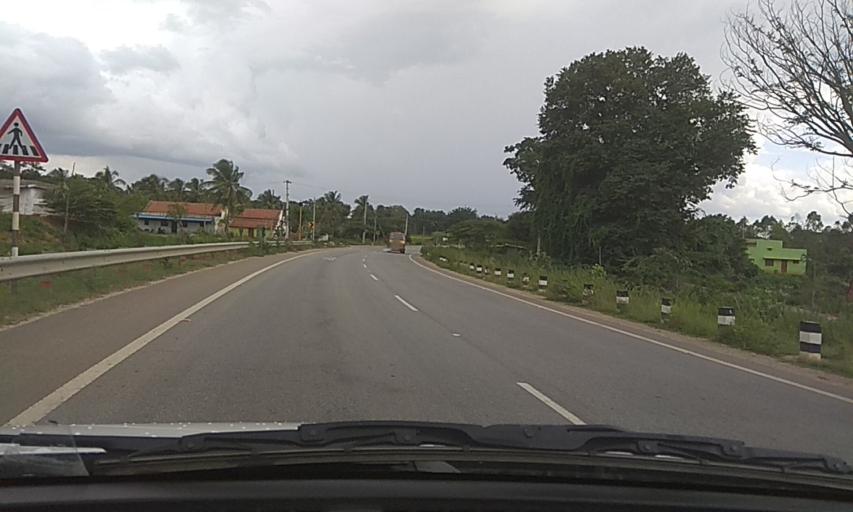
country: IN
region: Karnataka
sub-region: Tumkur
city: Kunigal
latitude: 12.8888
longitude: 77.0453
